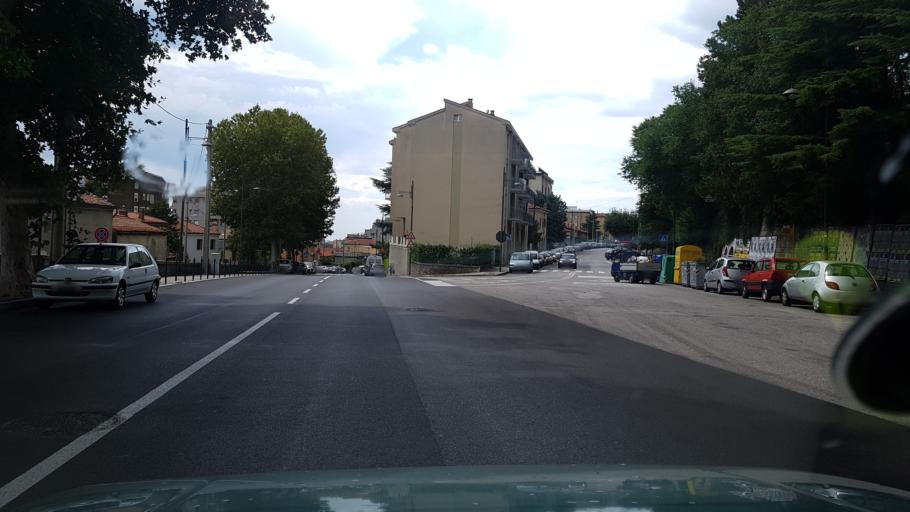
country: IT
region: Friuli Venezia Giulia
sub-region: Provincia di Trieste
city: Trieste
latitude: 45.6419
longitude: 13.8027
